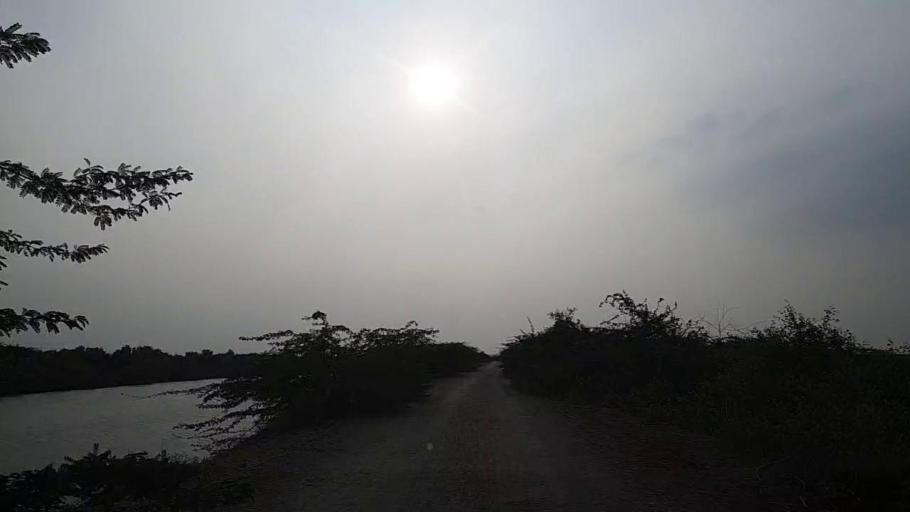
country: PK
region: Sindh
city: Mirpur Sakro
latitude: 24.6047
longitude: 67.5207
